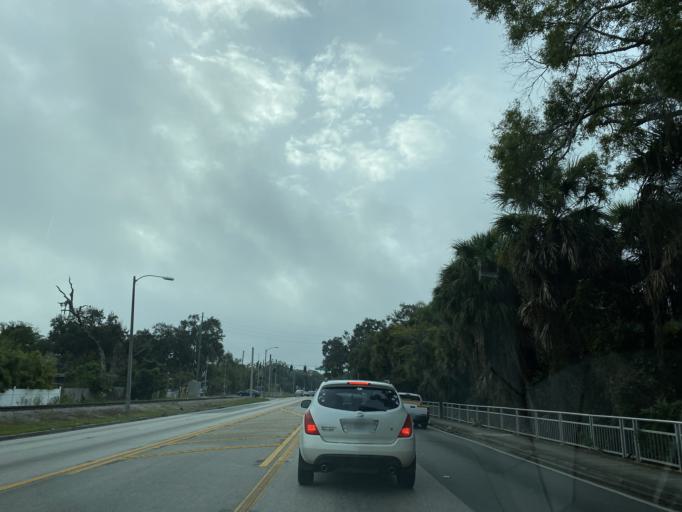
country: US
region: Florida
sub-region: Orange County
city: Orlando
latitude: 28.5609
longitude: -81.3979
